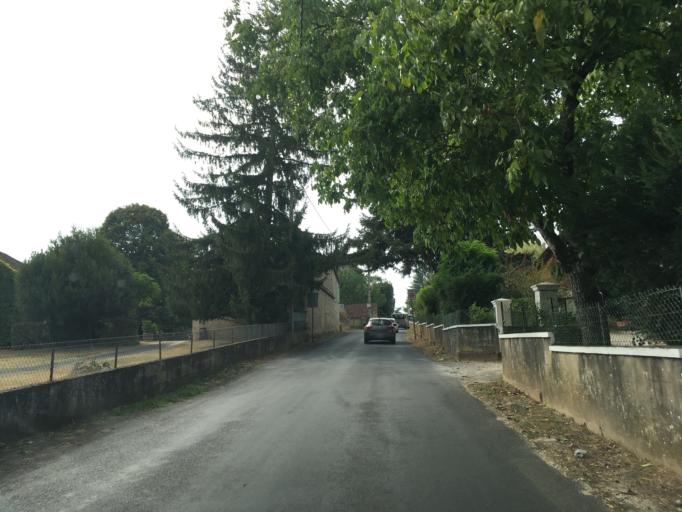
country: FR
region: Midi-Pyrenees
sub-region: Departement du Lot
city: Souillac
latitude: 44.8539
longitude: 1.5159
